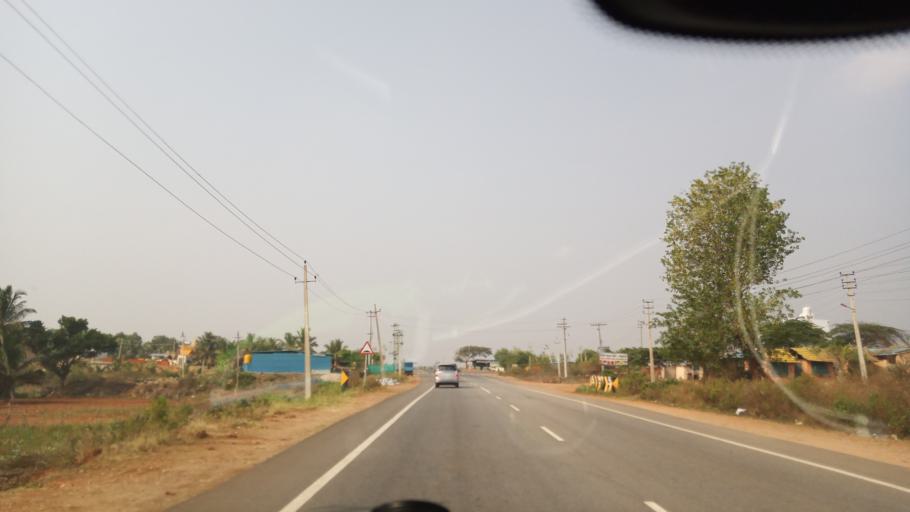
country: IN
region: Karnataka
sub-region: Mandya
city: Melukote
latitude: 12.7216
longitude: 76.7112
